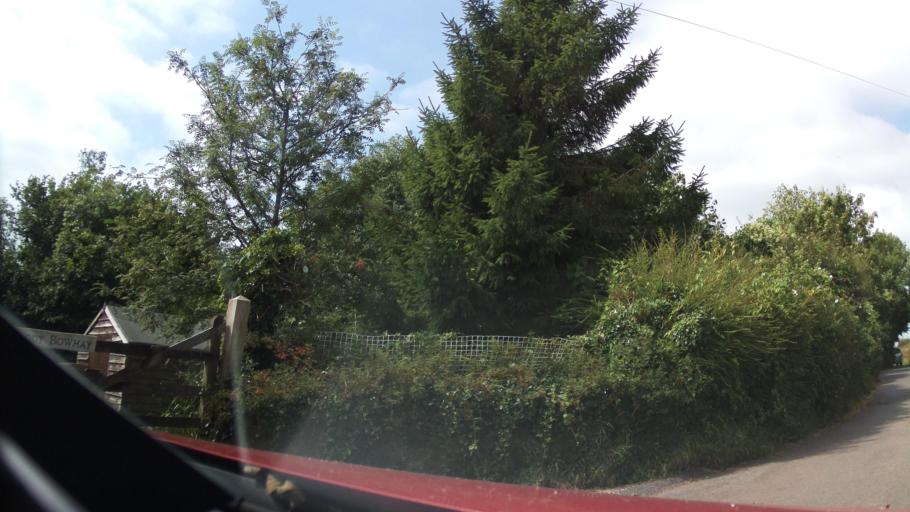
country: GB
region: England
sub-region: Devon
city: Marldon
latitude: 50.4195
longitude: -3.6335
